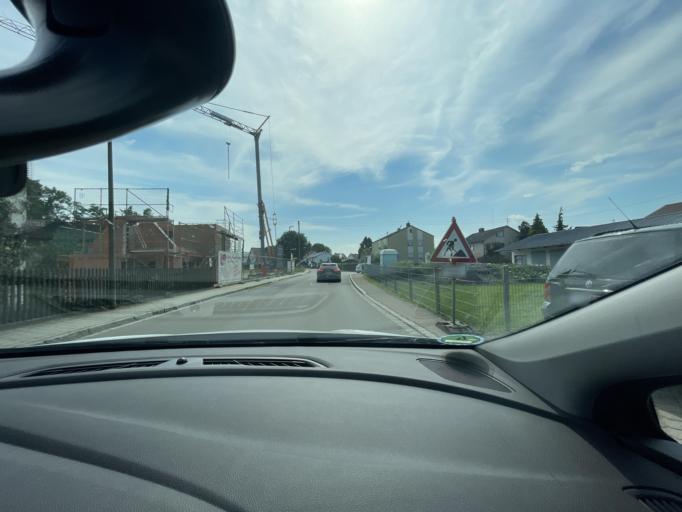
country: DE
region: Bavaria
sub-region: Upper Bavaria
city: Rohrmoos
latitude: 48.3202
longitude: 11.4123
